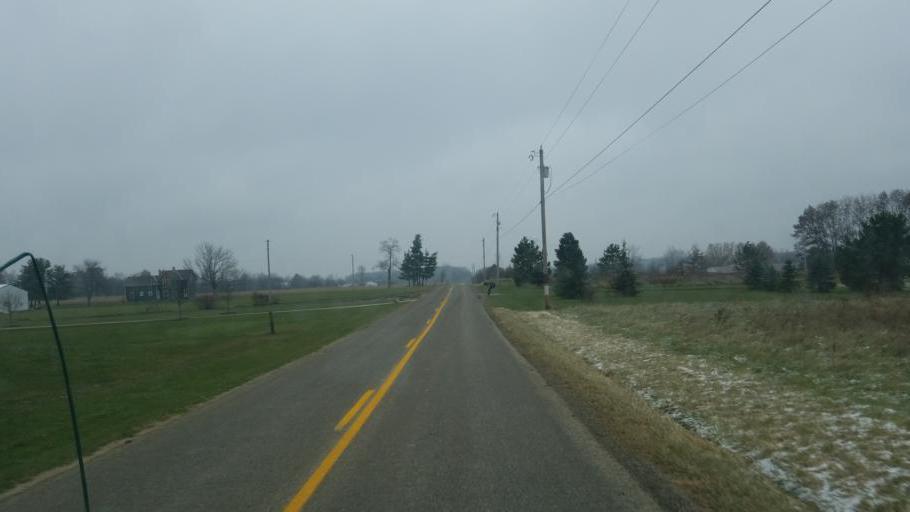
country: US
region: Ohio
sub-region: Huron County
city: New London
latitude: 41.0075
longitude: -82.3548
